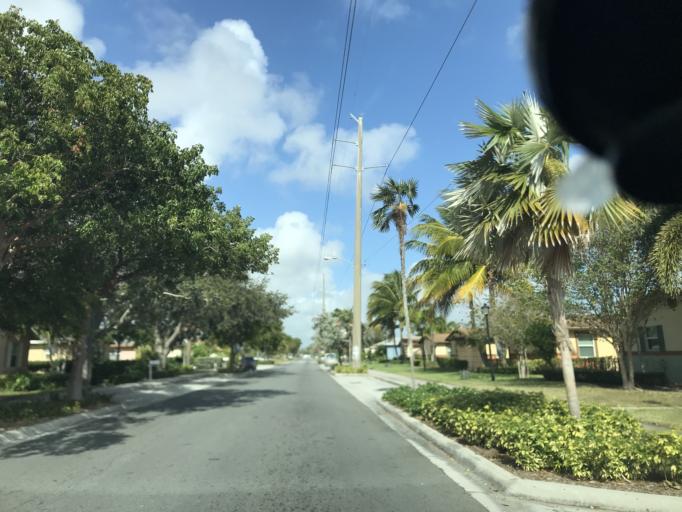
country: US
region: Florida
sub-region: Palm Beach County
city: Delray Beach
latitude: 26.4567
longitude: -80.0853
